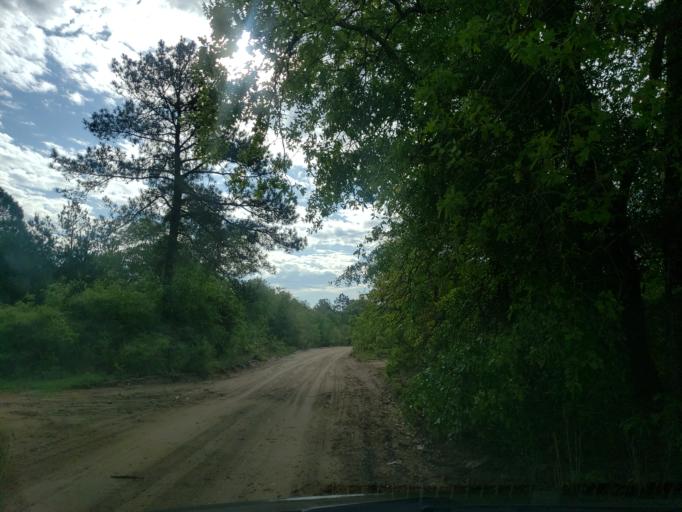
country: US
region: Georgia
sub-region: Emanuel County
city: Swainsboro
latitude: 32.4043
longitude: -82.3028
